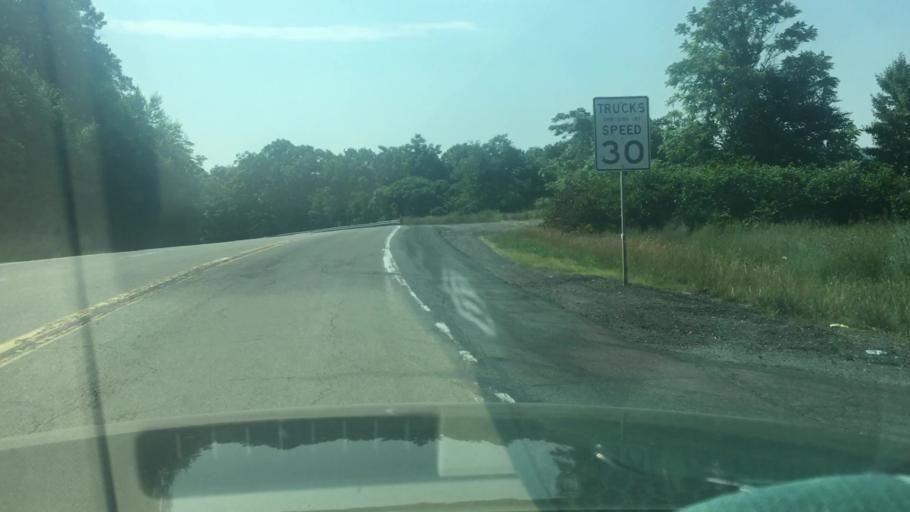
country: US
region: Pennsylvania
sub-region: Northumberland County
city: Mount Carmel
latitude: 40.7684
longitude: -76.3984
